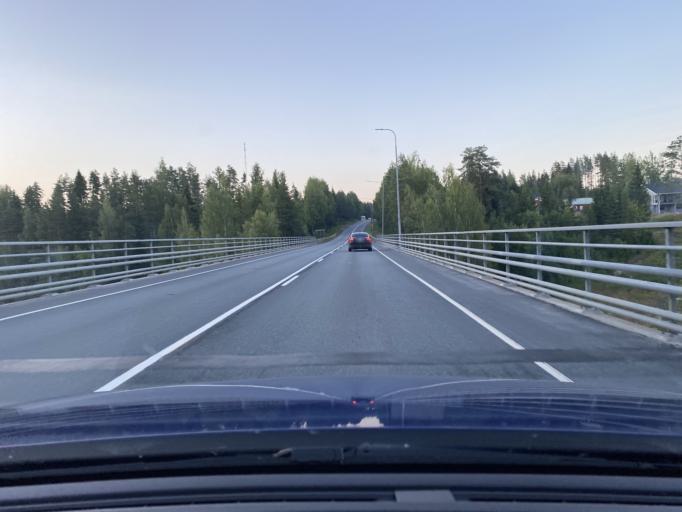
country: FI
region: Pirkanmaa
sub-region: Luoteis-Pirkanmaa
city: Ikaalinen
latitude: 61.8500
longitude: 22.9321
